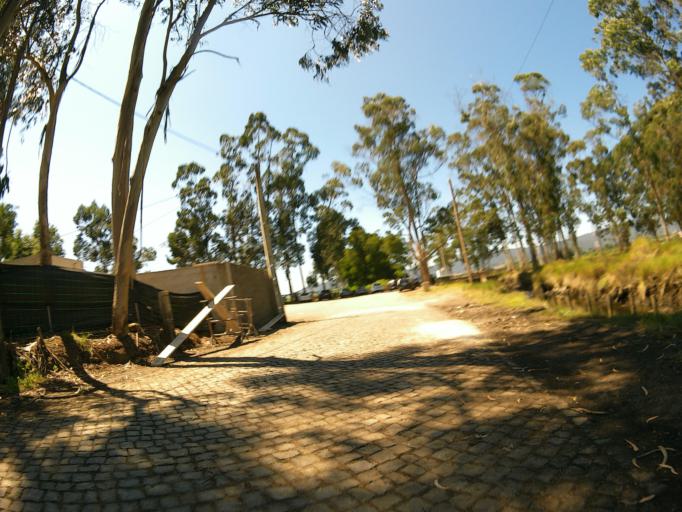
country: PT
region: Viana do Castelo
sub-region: Viana do Castelo
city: Darque
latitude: 41.6919
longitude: -8.7729
